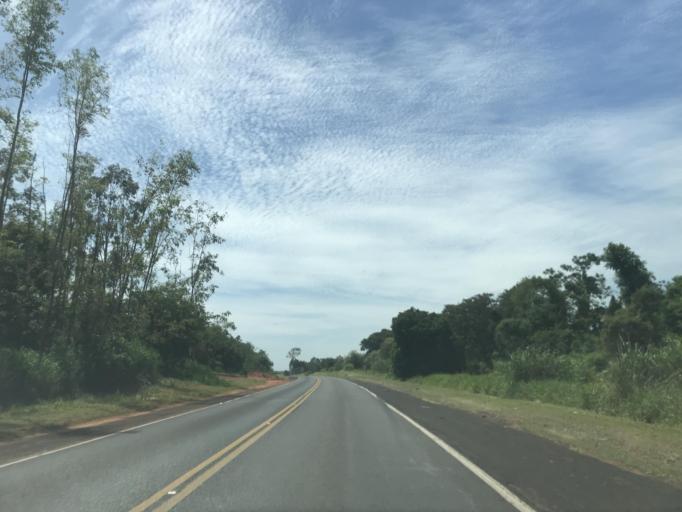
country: BR
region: Parana
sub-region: Paranavai
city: Nova Aurora
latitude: -22.9591
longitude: -52.6896
